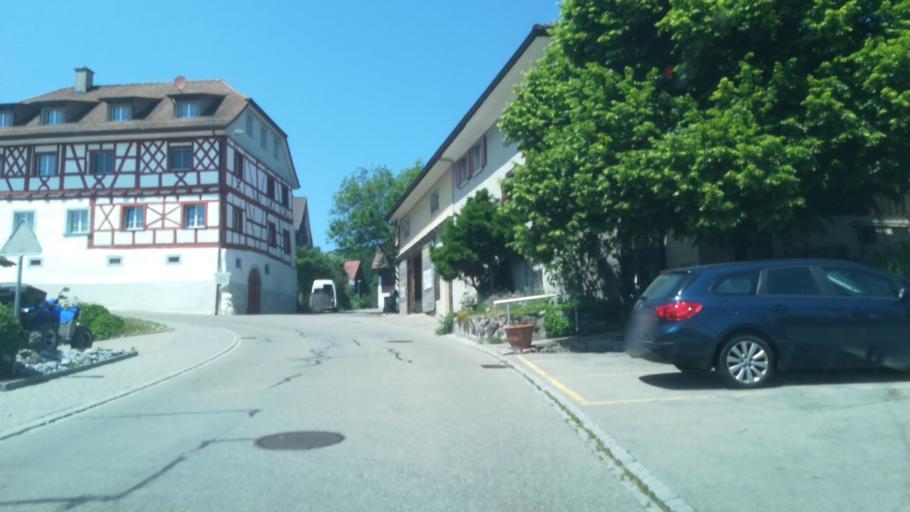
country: CH
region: Thurgau
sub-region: Frauenfeld District
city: Pfyn
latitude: 47.6231
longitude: 8.9382
